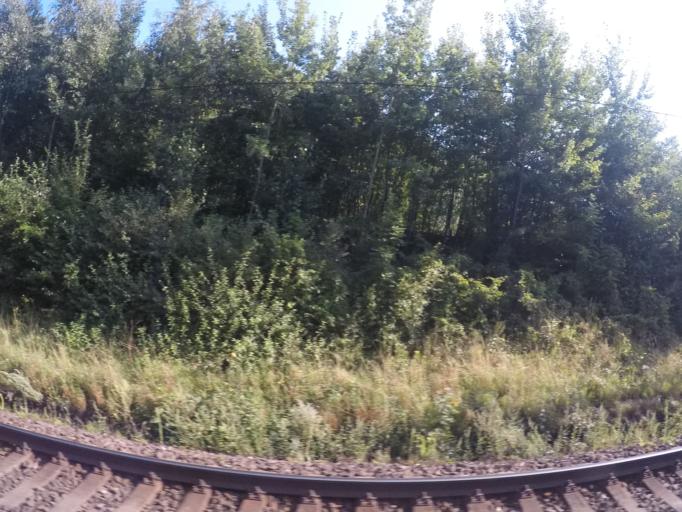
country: SK
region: Presovsky
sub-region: Okres Presov
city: Presov
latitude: 48.8531
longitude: 21.1641
